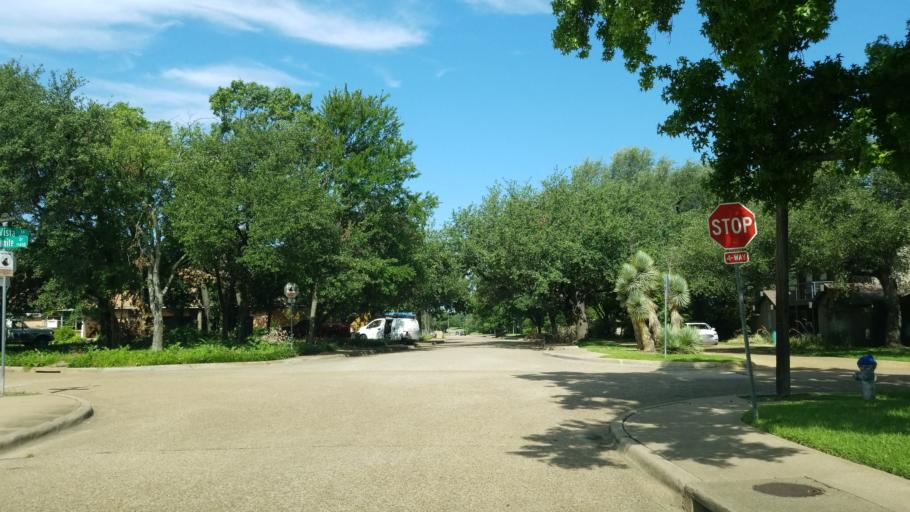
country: US
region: Texas
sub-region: Dallas County
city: Farmers Branch
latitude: 32.9042
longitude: -96.8432
